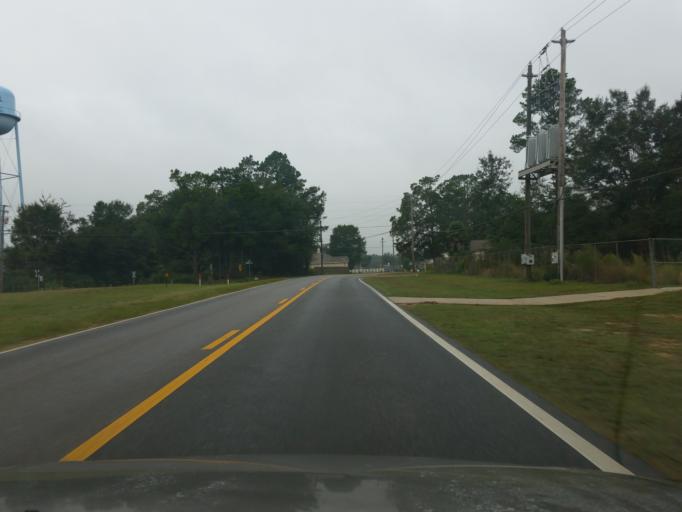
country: US
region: Florida
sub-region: Escambia County
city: Cantonment
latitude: 30.6056
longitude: -87.3436
